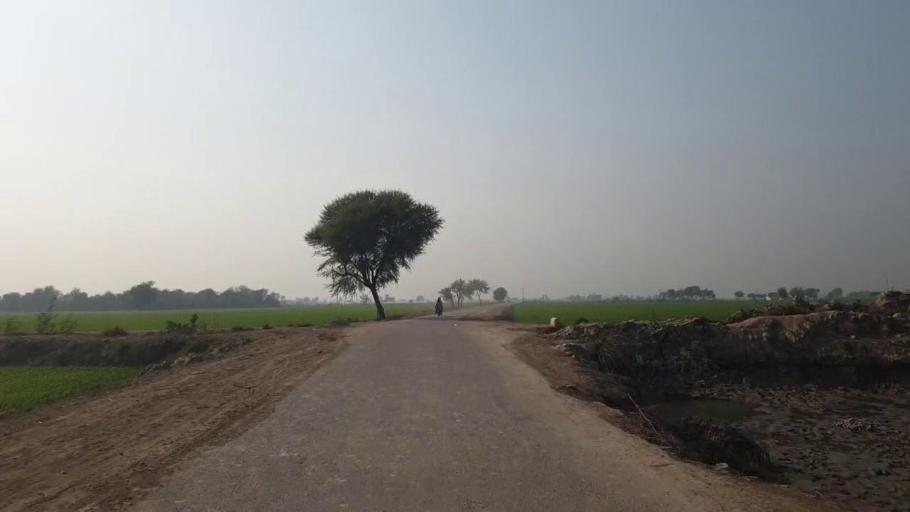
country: PK
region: Sindh
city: Shahdadpur
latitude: 25.9653
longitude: 68.5669
